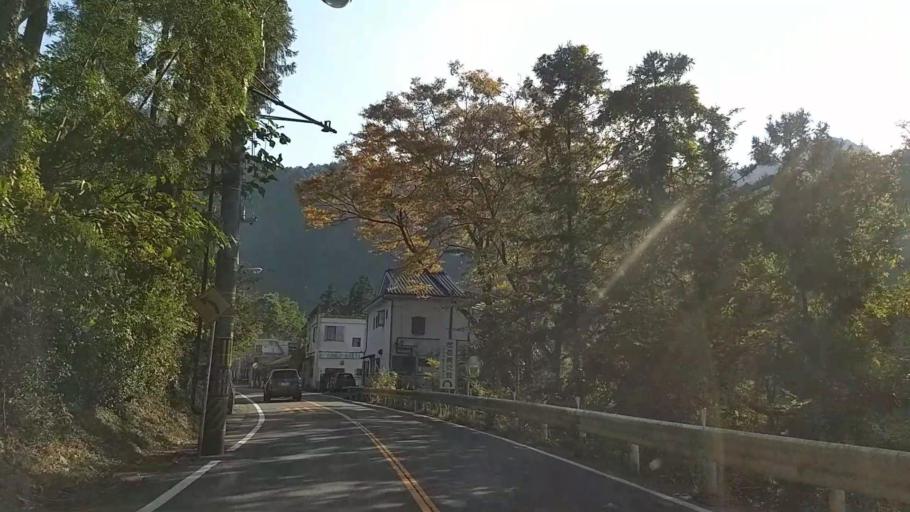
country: JP
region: Tokyo
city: Ome
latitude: 35.8020
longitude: 139.1765
